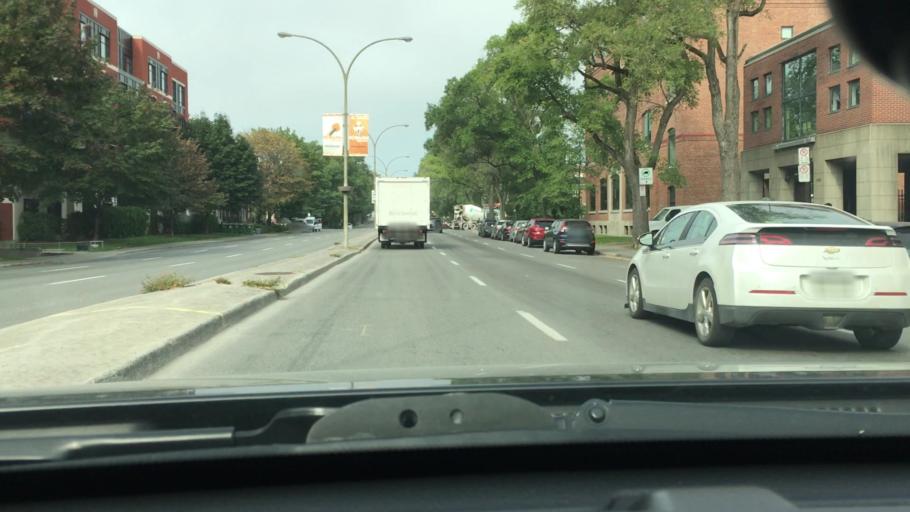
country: CA
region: Quebec
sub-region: Monteregie
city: Longueuil
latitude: 45.5510
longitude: -73.5432
